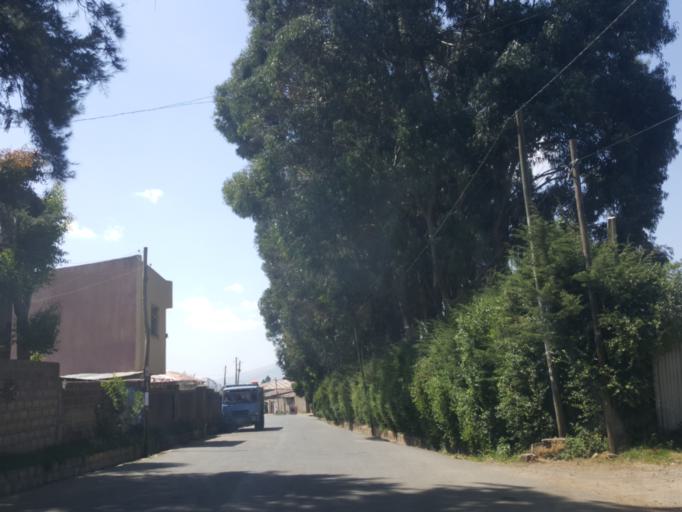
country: ET
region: Adis Abeba
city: Addis Ababa
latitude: 9.0592
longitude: 38.7324
